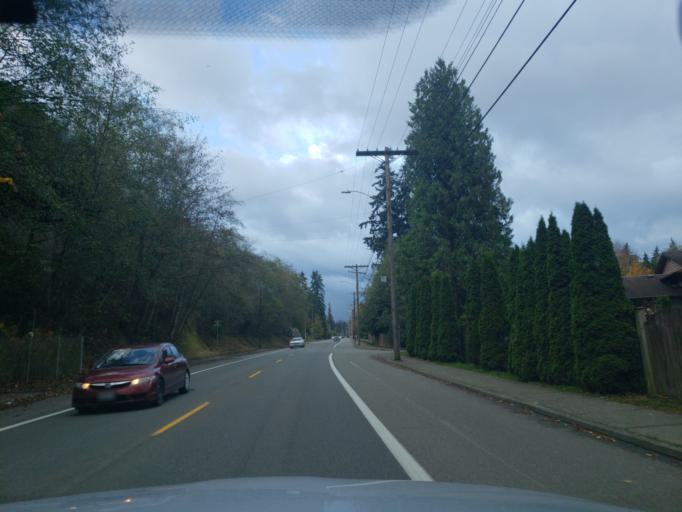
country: US
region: Washington
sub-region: Snohomish County
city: Everett
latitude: 47.9507
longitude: -122.2460
